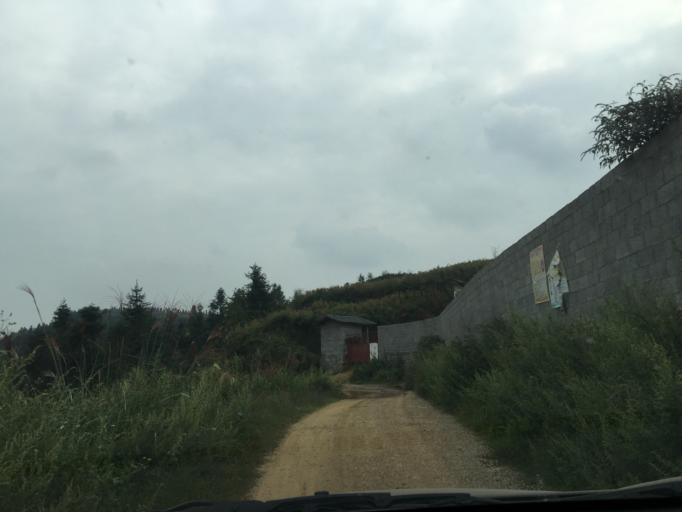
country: CN
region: Guangxi Zhuangzu Zizhiqu
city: Xinzhou
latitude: 25.5444
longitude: 105.5329
